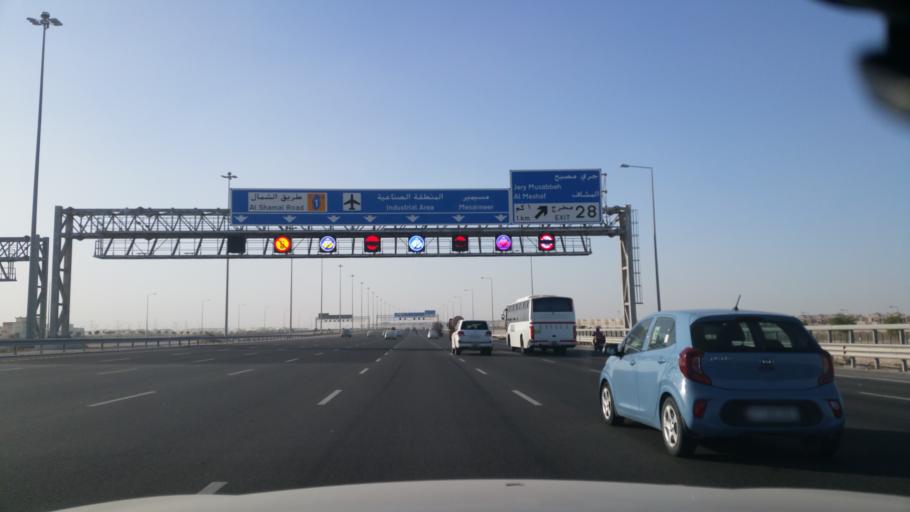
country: QA
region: Al Wakrah
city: Al Wukayr
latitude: 25.1701
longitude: 51.5600
